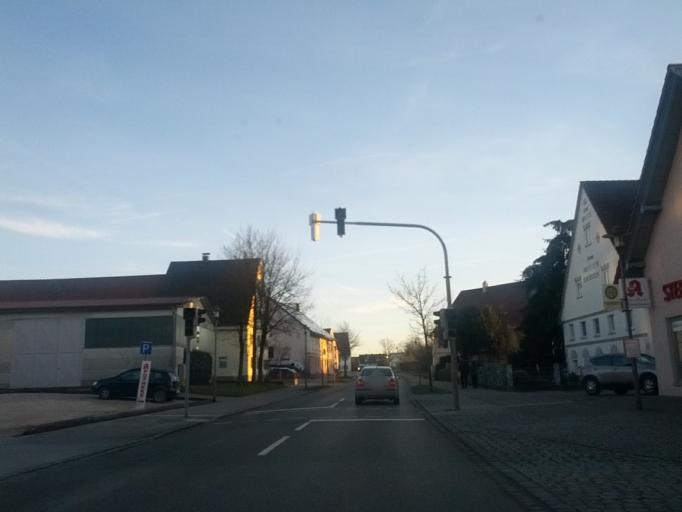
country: DE
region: Bavaria
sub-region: Swabia
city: Heimertingen
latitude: 48.0394
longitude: 10.1538
